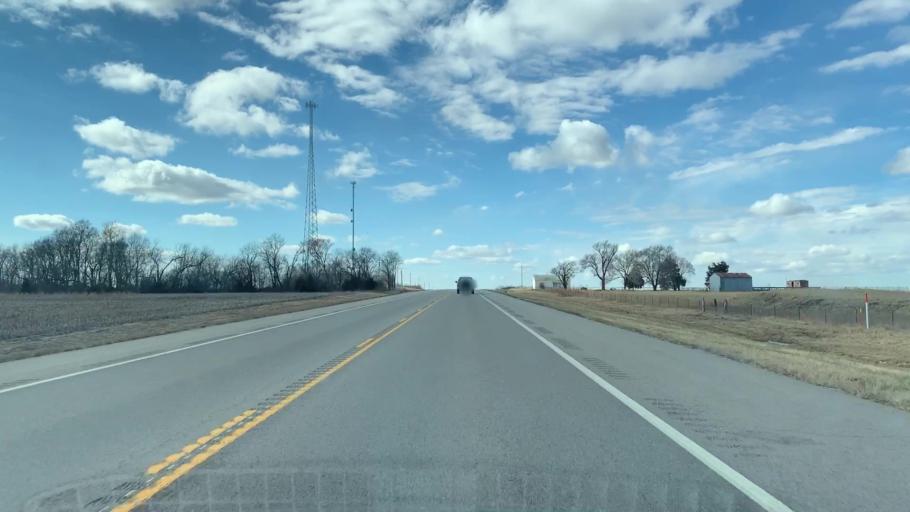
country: US
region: Kansas
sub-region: Labette County
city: Oswego
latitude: 37.3401
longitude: -95.0232
